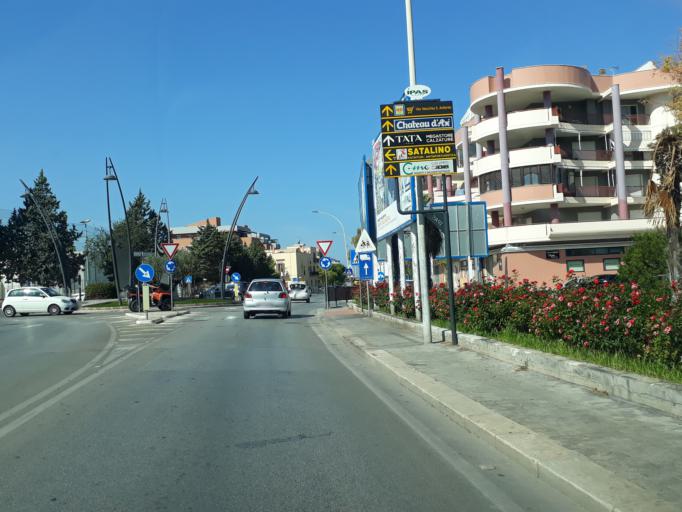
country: IT
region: Apulia
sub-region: Provincia di Bari
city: Monopoli
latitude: 40.9481
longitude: 17.2910
